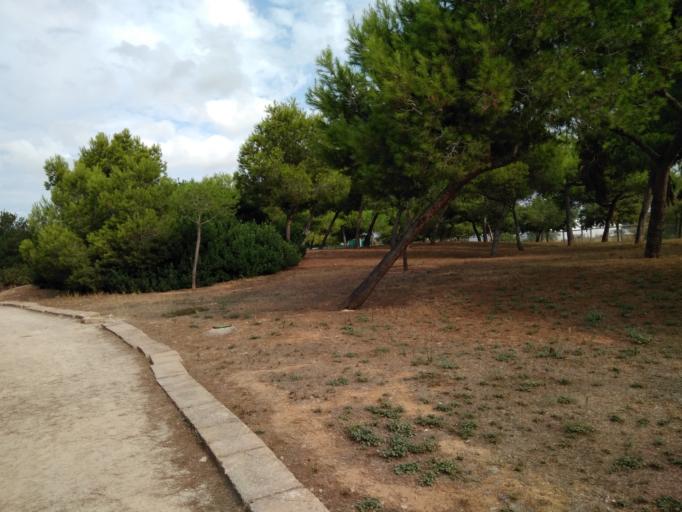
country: ES
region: Balearic Islands
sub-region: Illes Balears
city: s'Arenal
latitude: 39.5290
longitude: 2.7383
